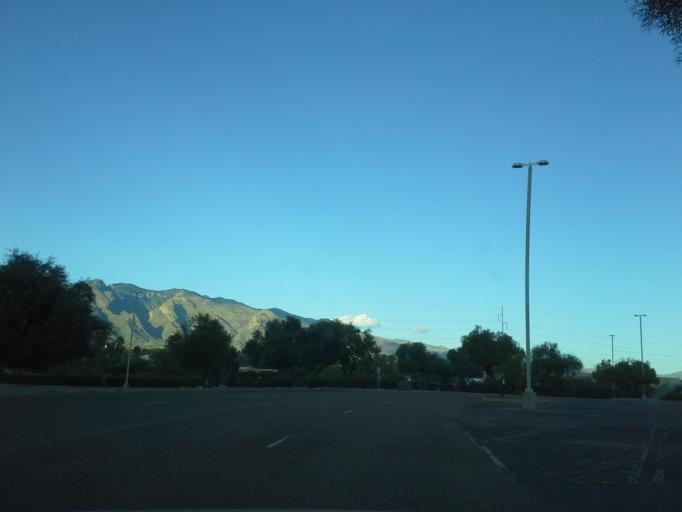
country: US
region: Arizona
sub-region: Pima County
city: Flowing Wells
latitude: 32.2912
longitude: -110.9758
